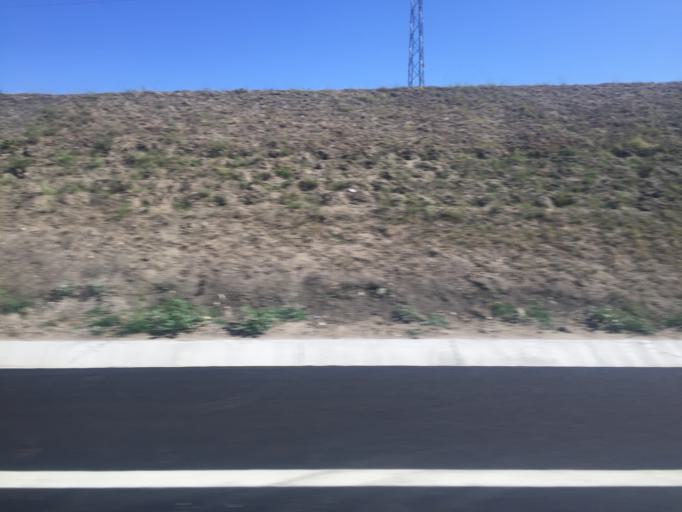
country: TR
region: Bursa
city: Gorukle
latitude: 40.2529
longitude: 28.7442
